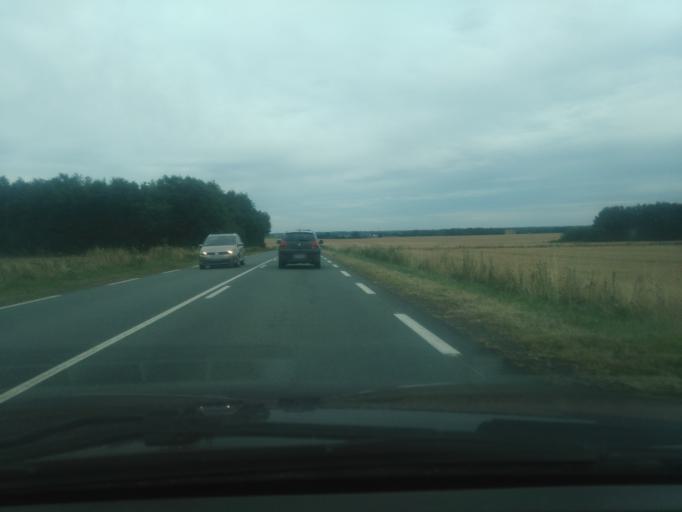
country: FR
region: Poitou-Charentes
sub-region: Departement de la Vienne
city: Saint-Savin
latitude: 46.5719
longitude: 0.8173
